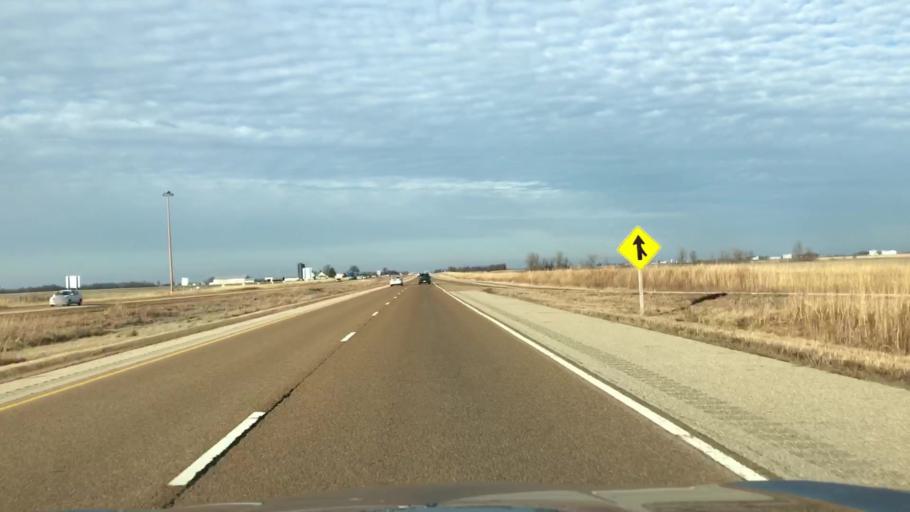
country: US
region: Illinois
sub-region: Montgomery County
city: Raymond
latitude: 39.3246
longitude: -89.6425
